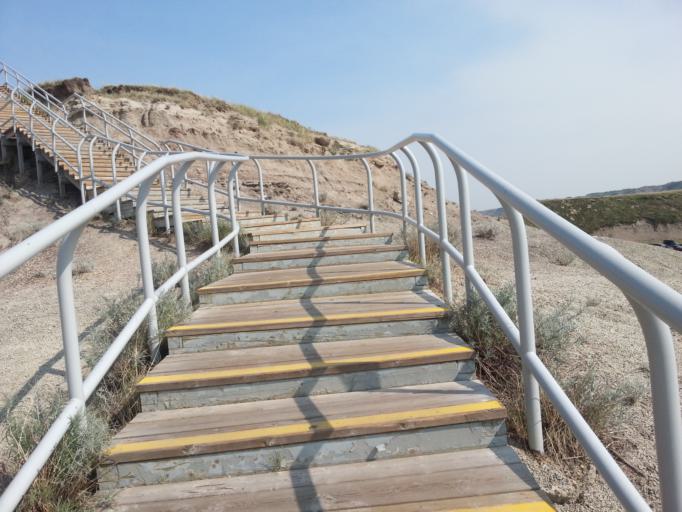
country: CA
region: Alberta
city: Three Hills
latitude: 51.4791
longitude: -112.7885
